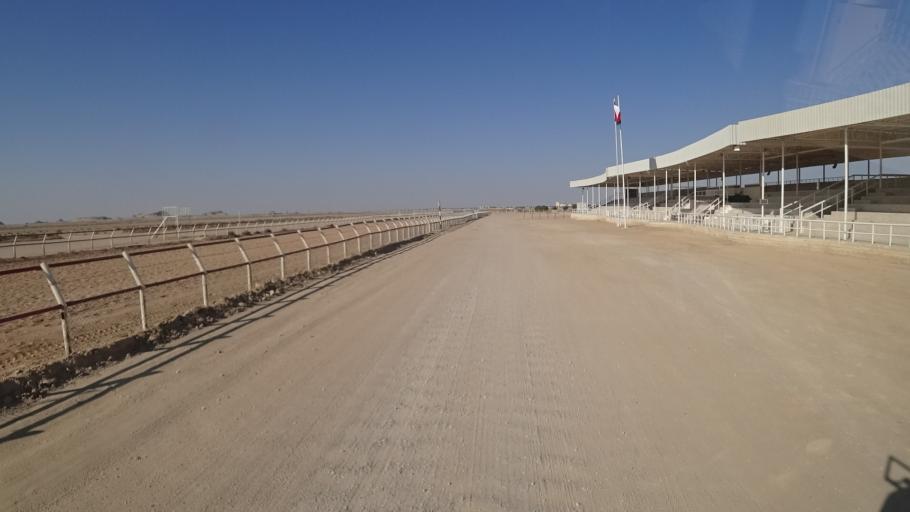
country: OM
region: Zufar
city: Salalah
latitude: 17.5928
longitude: 54.0253
